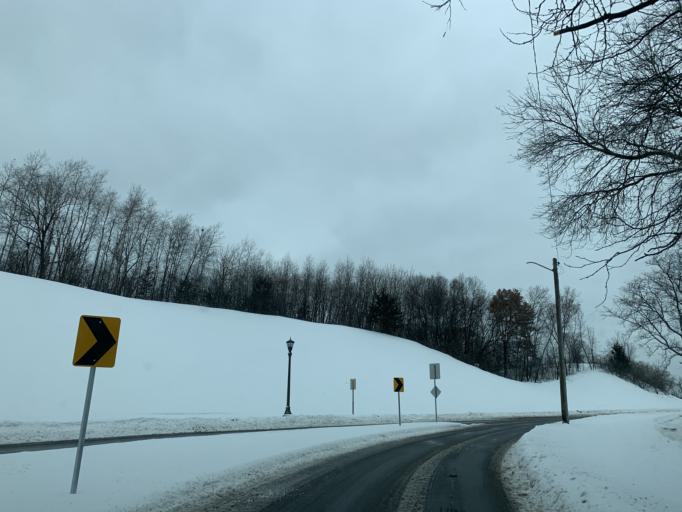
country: US
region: Minnesota
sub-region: Ramsey County
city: Little Canada
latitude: 44.9887
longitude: -93.1122
